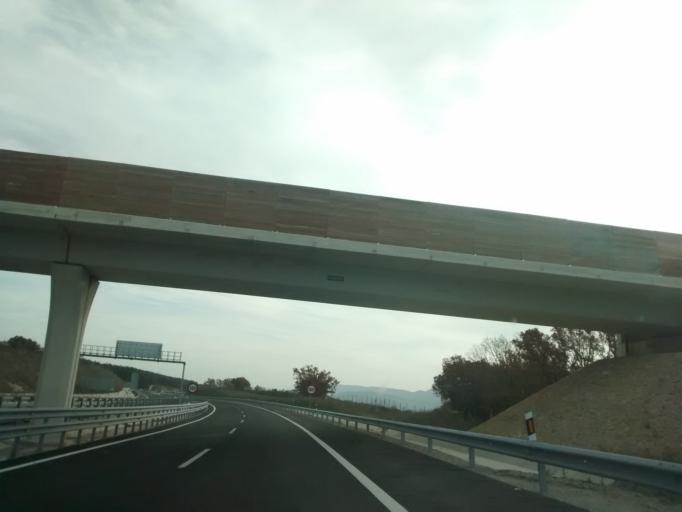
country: ES
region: Navarre
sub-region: Provincia de Navarra
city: Yesa
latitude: 42.6217
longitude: -1.1637
